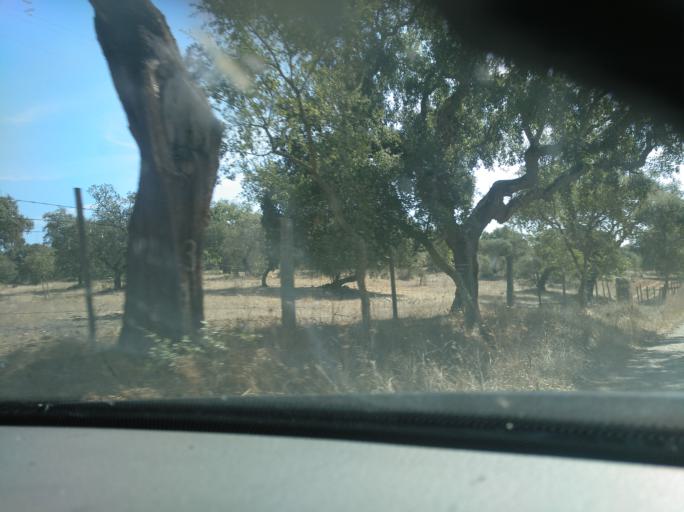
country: PT
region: Evora
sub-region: Arraiolos
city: Arraiolos
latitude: 38.7021
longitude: -8.0963
